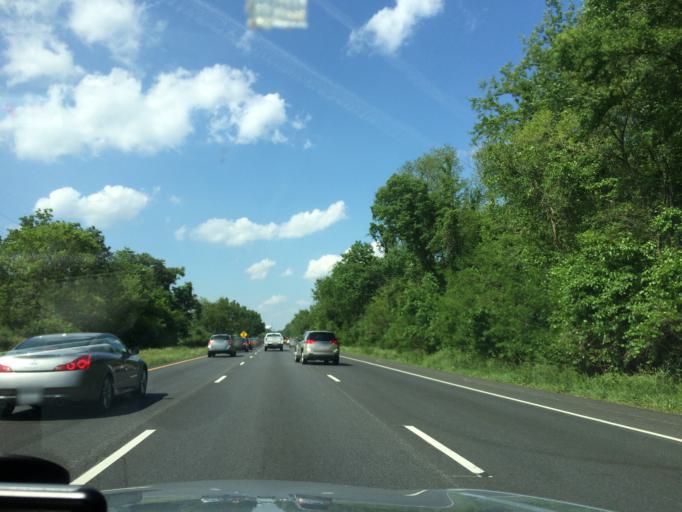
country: US
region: Maryland
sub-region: Anne Arundel County
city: Crofton
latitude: 39.0056
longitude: -76.6990
